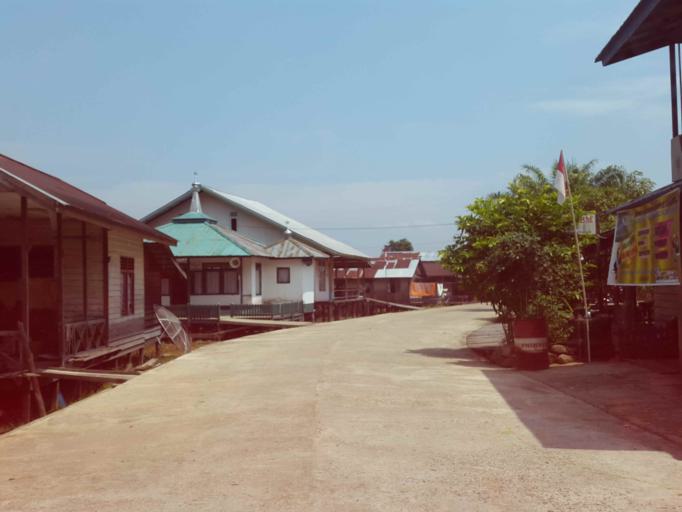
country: MY
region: Sarawak
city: Simanggang
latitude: 1.0326
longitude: 112.2288
